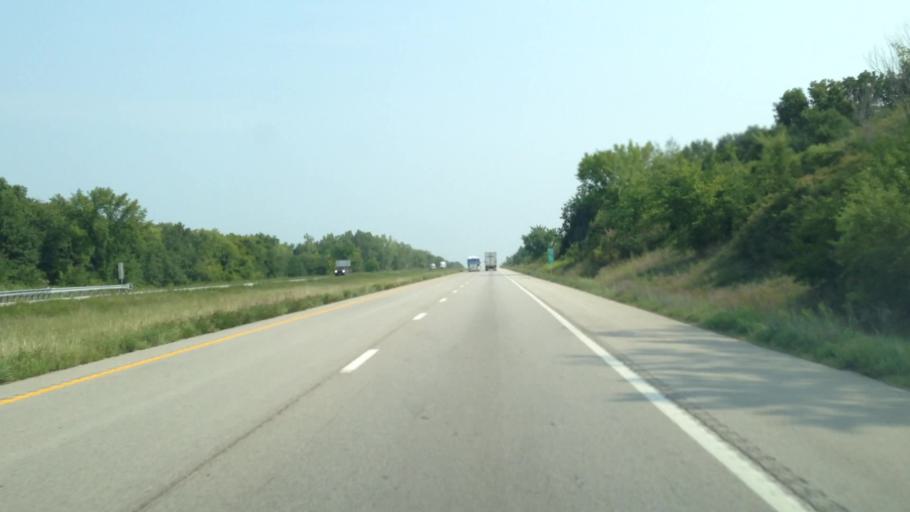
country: US
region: Missouri
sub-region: Clinton County
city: Cameron
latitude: 39.7747
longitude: -94.2116
